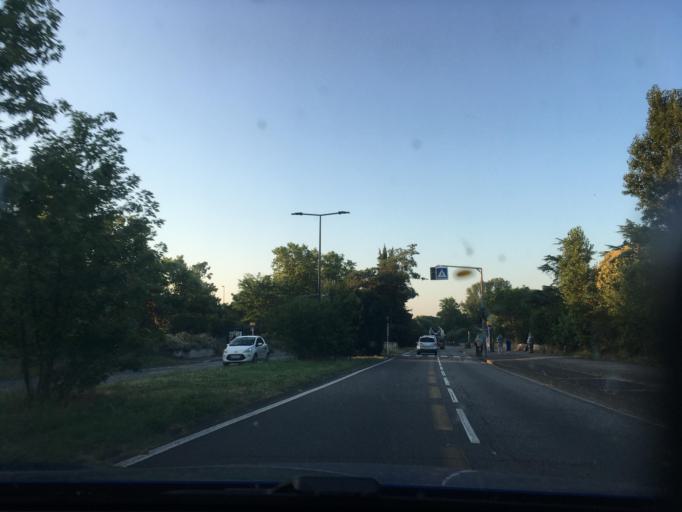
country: FR
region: Midi-Pyrenees
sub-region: Departement de la Haute-Garonne
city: Portet-sur-Garonne
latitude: 43.5774
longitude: 1.3948
